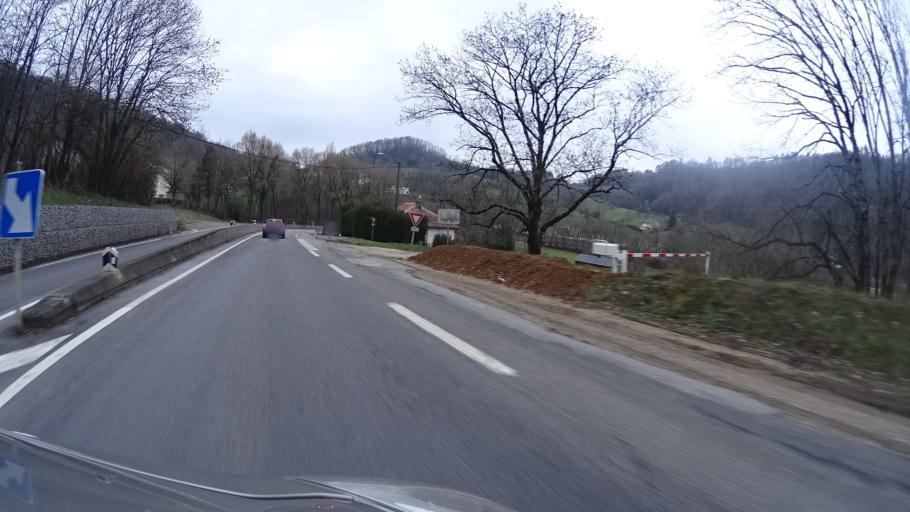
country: FR
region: Franche-Comte
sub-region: Departement du Doubs
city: Morre
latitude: 47.2215
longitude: 6.0638
